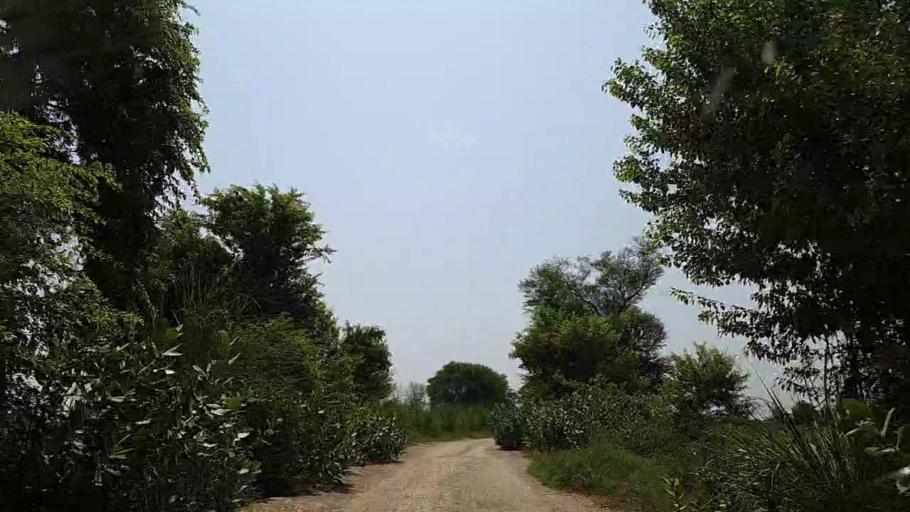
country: PK
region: Sindh
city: Adilpur
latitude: 27.9317
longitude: 69.3886
